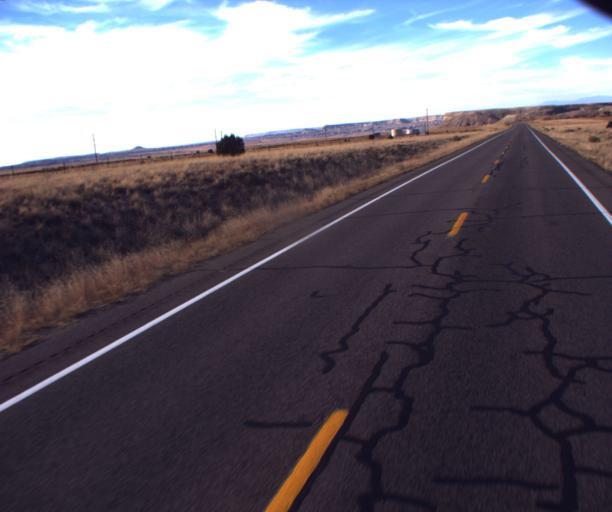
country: US
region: New Mexico
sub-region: San Juan County
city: Shiprock
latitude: 36.9061
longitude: -109.0702
